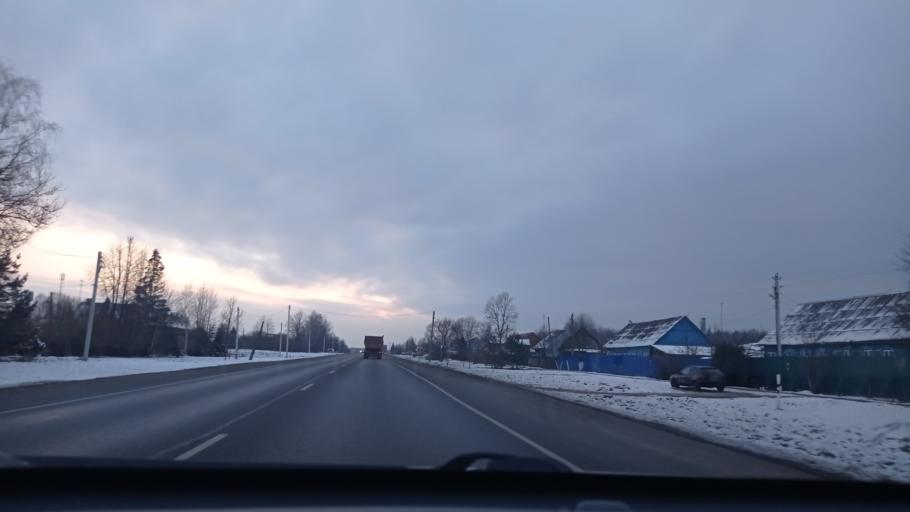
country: RU
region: Moskovskaya
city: Ateptsevo
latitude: 55.1936
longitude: 36.9137
